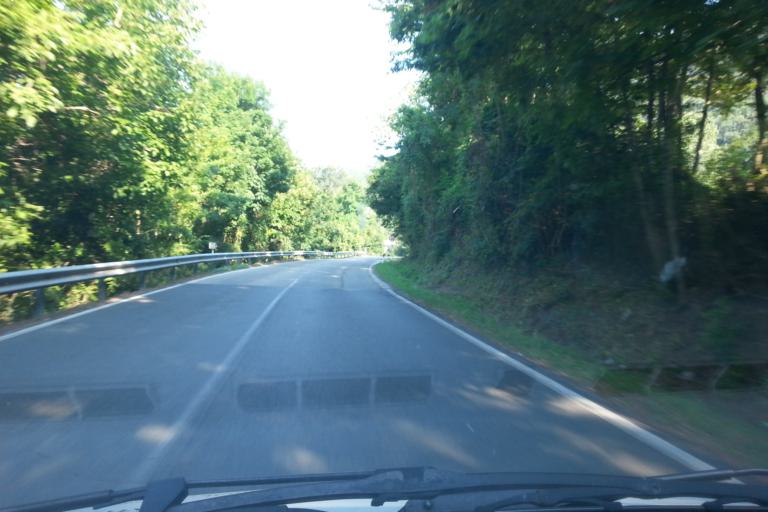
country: IT
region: Piedmont
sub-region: Provincia di Torino
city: San Giorio
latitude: 45.1231
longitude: 7.1932
